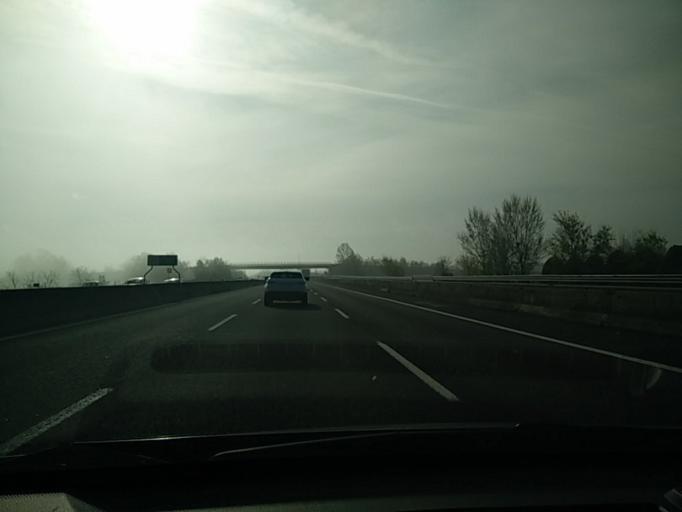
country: IT
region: Emilia-Romagna
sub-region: Provincia di Bologna
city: Ozzano dell'Emilia
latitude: 44.4679
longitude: 11.4813
